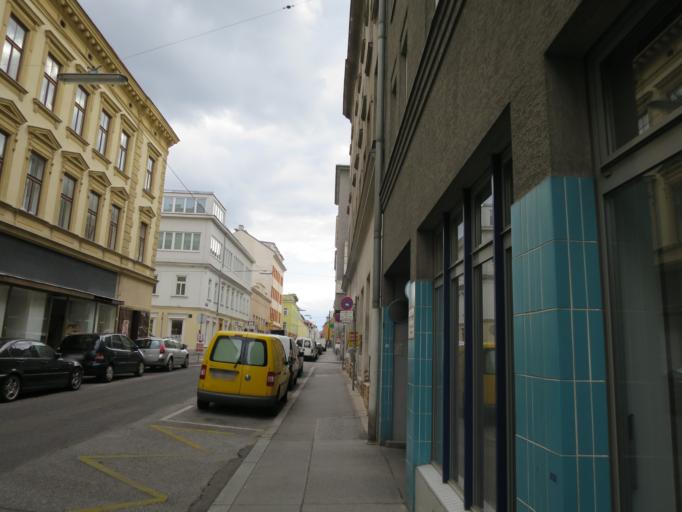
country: AT
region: Vienna
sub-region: Wien Stadt
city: Vienna
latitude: 48.2152
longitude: 16.3317
